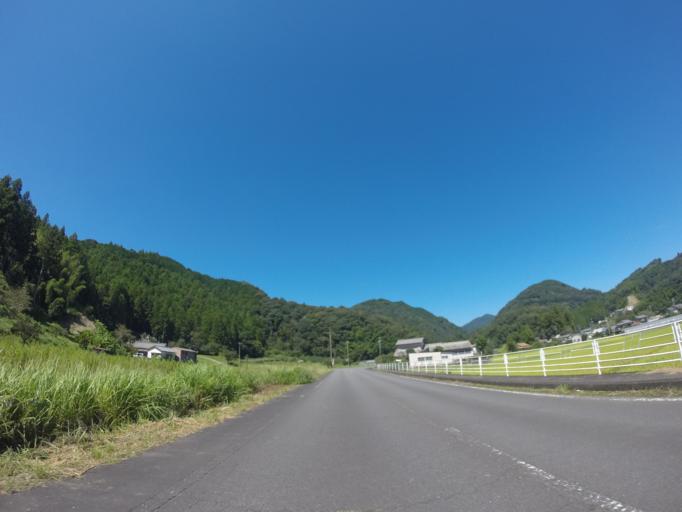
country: JP
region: Shizuoka
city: Fujieda
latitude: 34.9111
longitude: 138.1921
